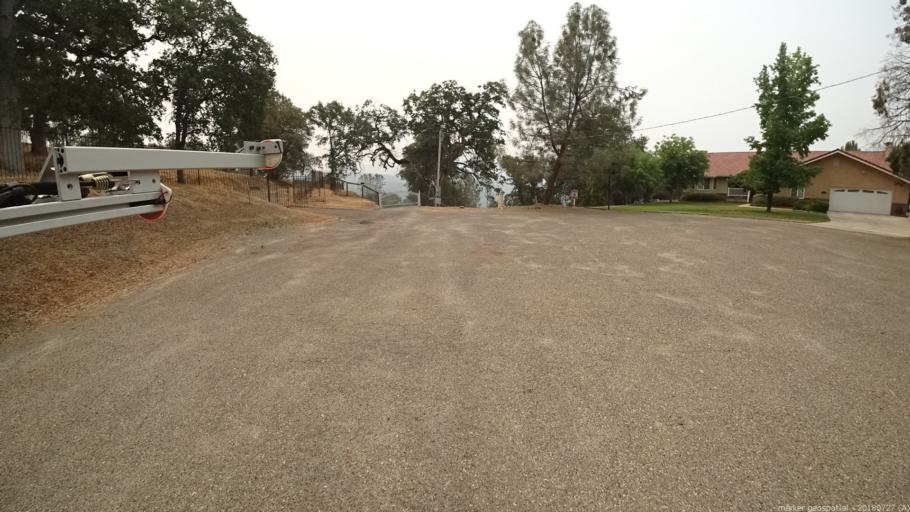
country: US
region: California
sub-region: Madera County
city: Oakhurst
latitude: 37.3385
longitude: -119.6286
